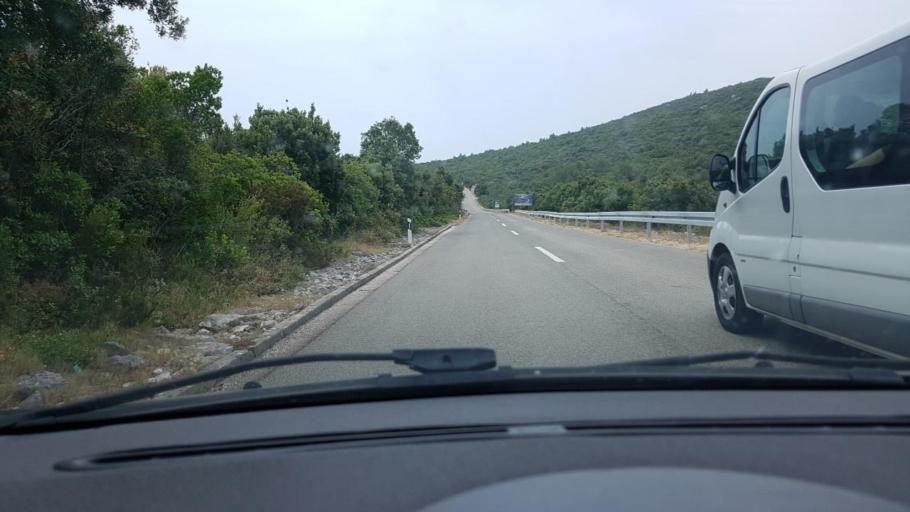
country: HR
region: Dubrovacko-Neretvanska
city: Smokvica
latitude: 42.9483
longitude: 16.9684
